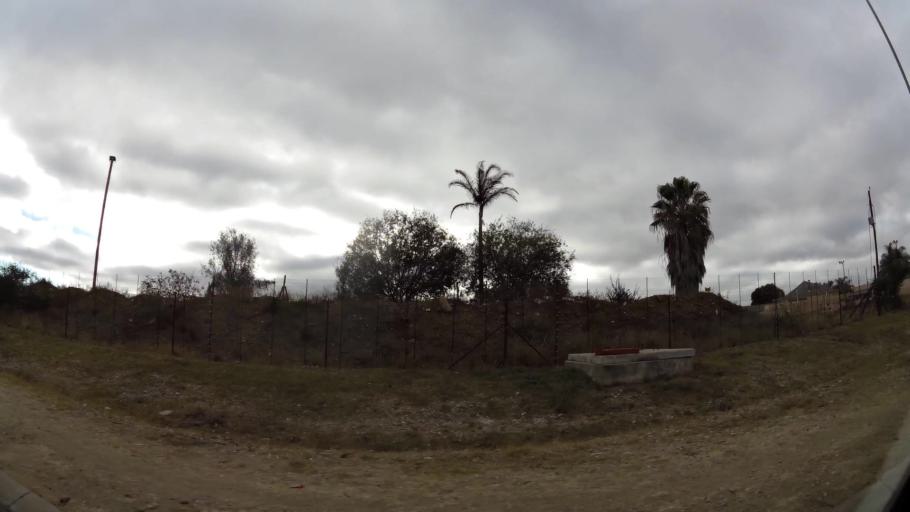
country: ZA
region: Limpopo
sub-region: Capricorn District Municipality
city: Polokwane
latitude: -23.9260
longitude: 29.4492
